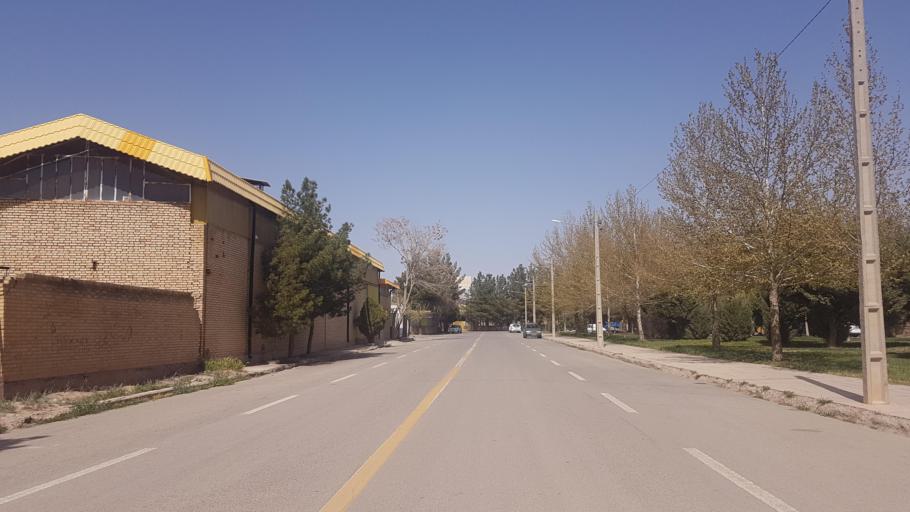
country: IR
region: Razavi Khorasan
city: Mashhad
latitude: 36.4587
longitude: 59.6658
